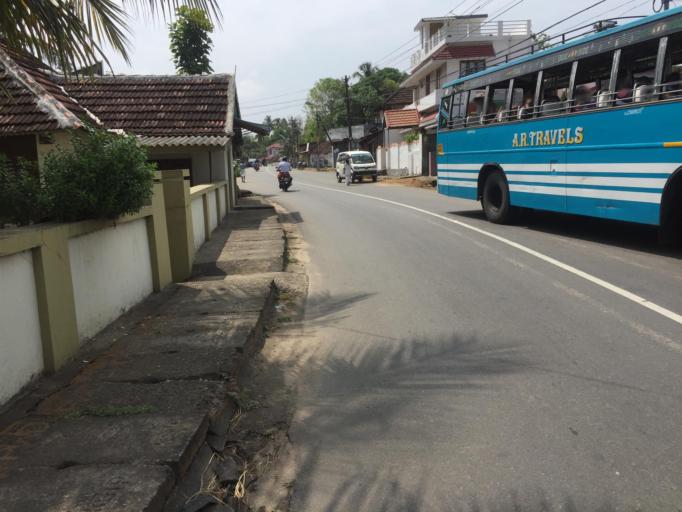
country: IN
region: Kerala
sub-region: Palakkad district
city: Chittur
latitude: 10.6828
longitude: 76.7125
